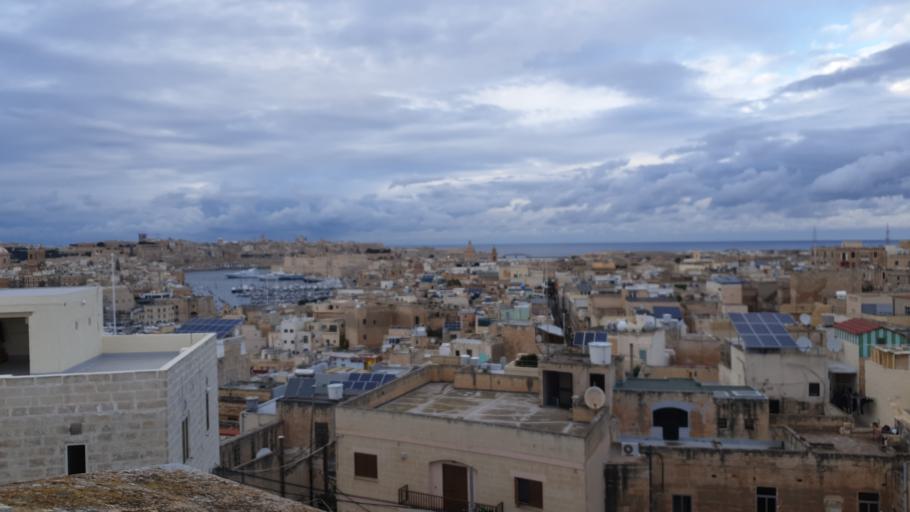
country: MT
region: Bormla
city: Cospicua
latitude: 35.8808
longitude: 14.5233
